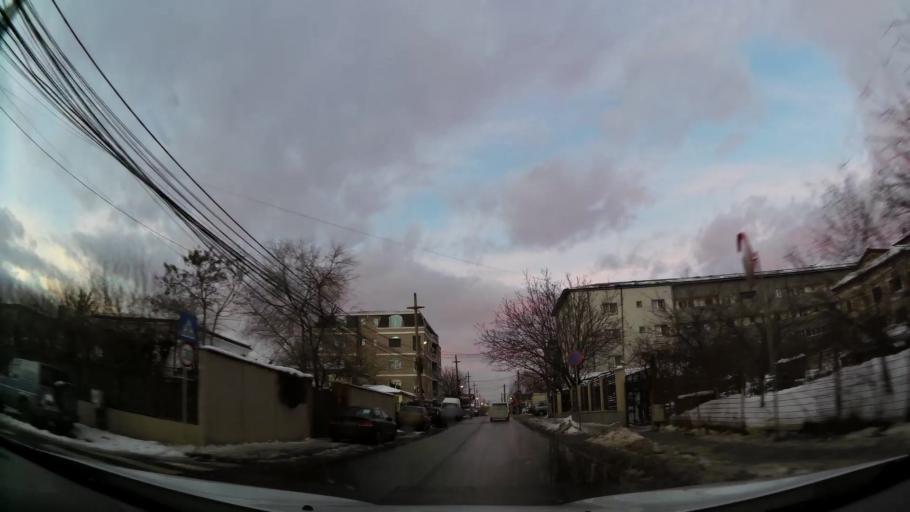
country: RO
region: Ilfov
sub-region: Comuna Popesti-Leordeni
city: Popesti-Leordeni
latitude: 44.3774
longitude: 26.1576
